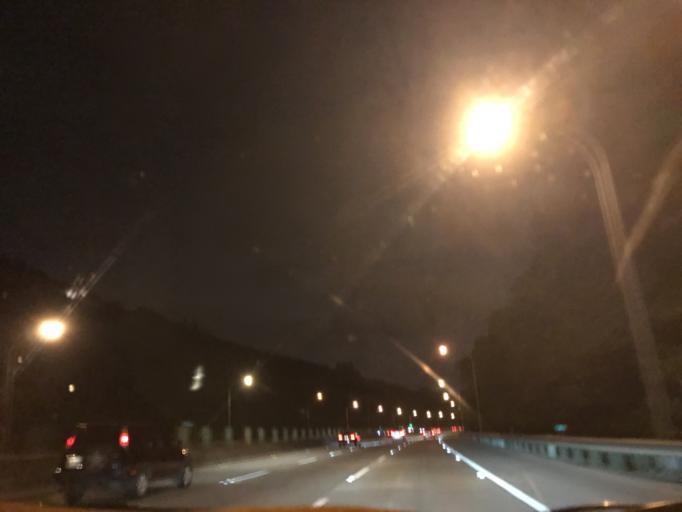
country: TW
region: Taiwan
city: Daxi
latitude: 24.8464
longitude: 121.2000
